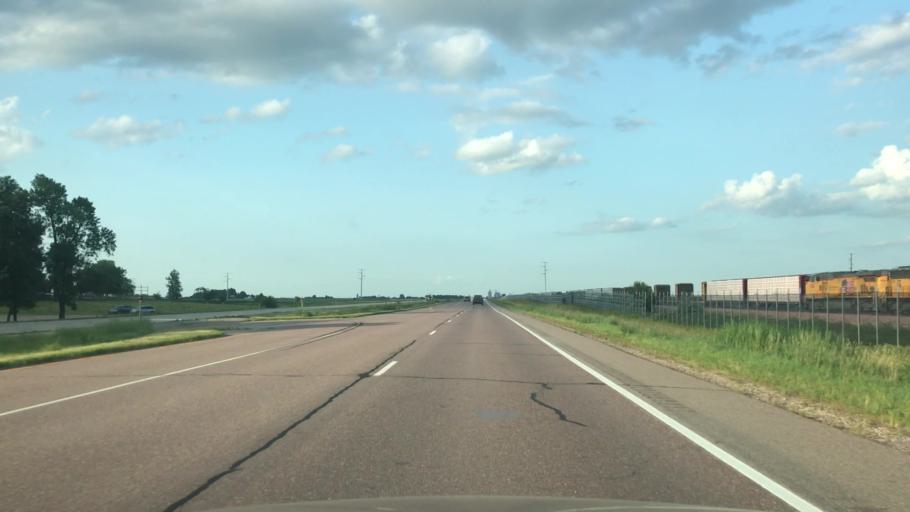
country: US
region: Minnesota
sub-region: Nobles County
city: Worthington
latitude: 43.6656
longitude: -95.5222
